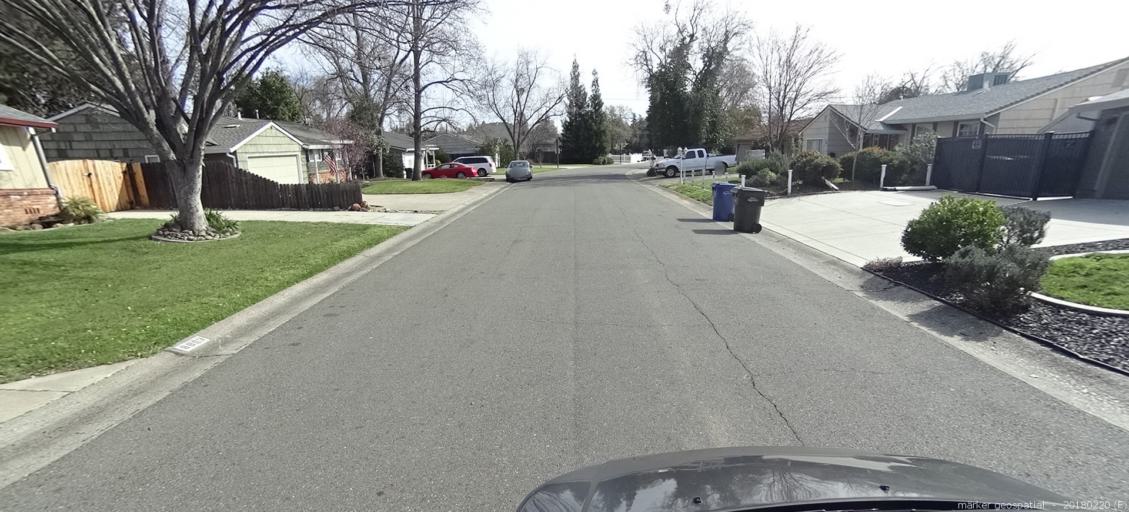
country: US
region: California
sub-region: Sacramento County
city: Orangevale
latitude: 38.6763
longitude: -121.2275
